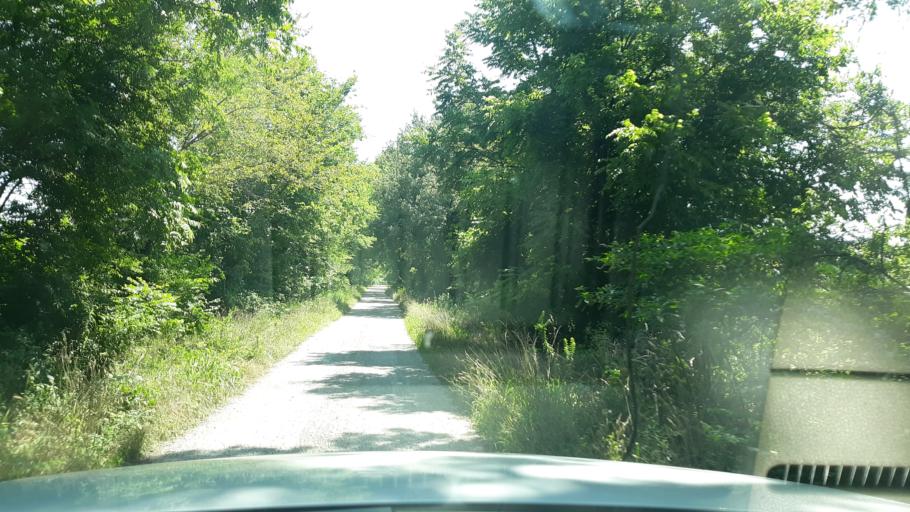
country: US
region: Illinois
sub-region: Saline County
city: Harrisburg
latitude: 37.8514
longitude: -88.6100
